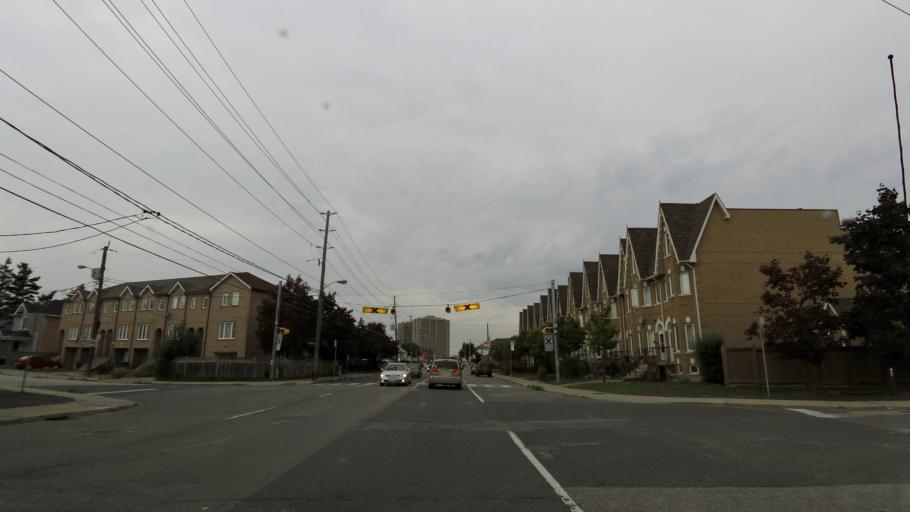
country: CA
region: Ontario
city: Etobicoke
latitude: 43.6946
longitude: -79.5062
